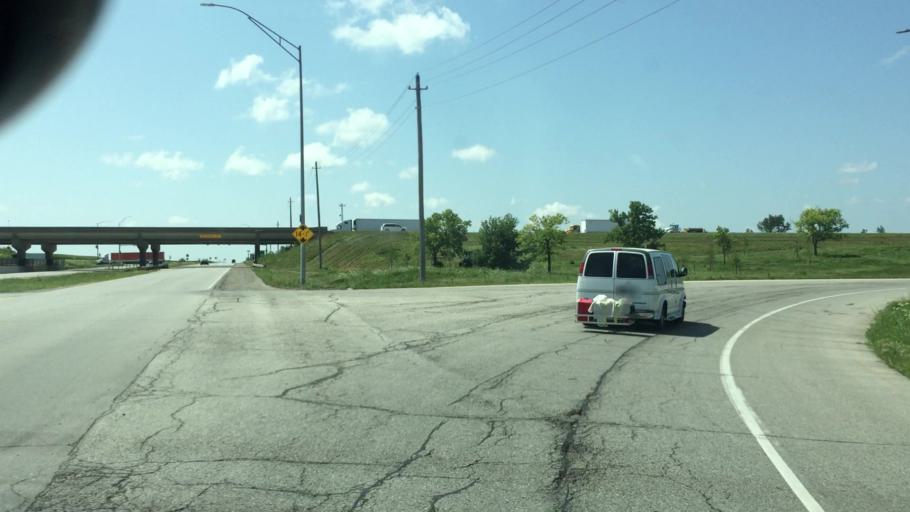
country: US
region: Iowa
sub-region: Poweshiek County
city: Grinnell
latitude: 41.6979
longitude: -92.7273
